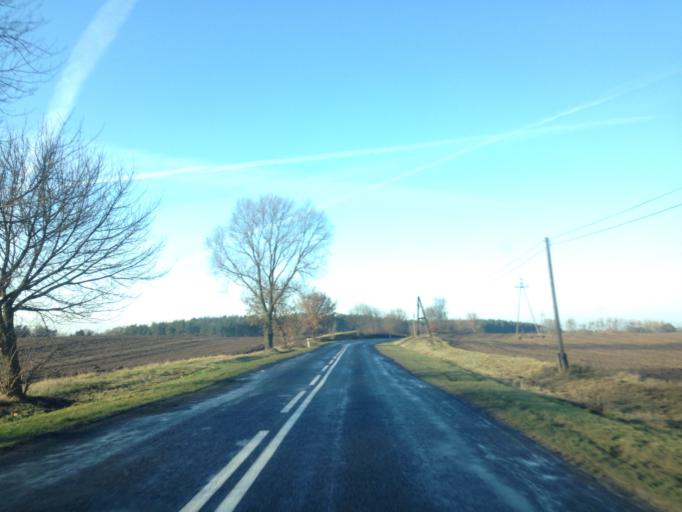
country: PL
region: Kujawsko-Pomorskie
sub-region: Powiat brodnicki
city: Bobrowo
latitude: 53.3278
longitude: 19.2414
